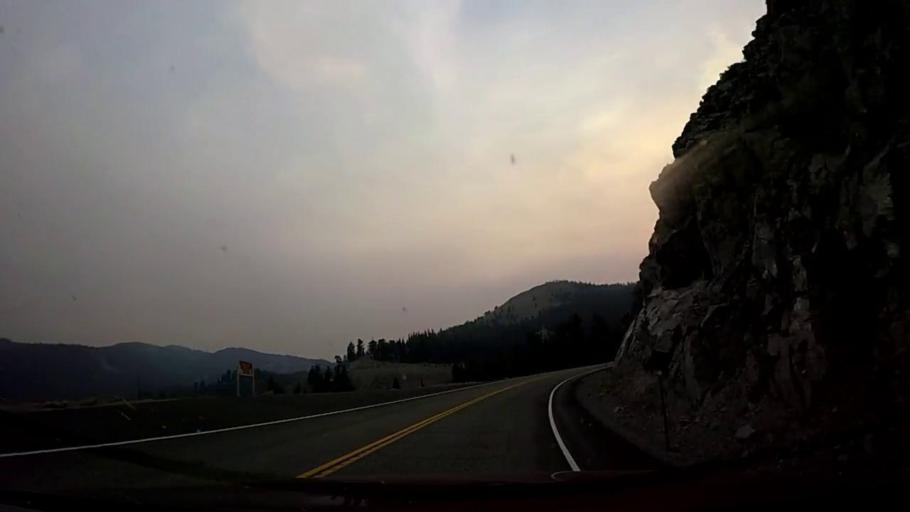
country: US
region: Idaho
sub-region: Blaine County
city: Ketchum
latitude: 43.8821
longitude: -114.6969
